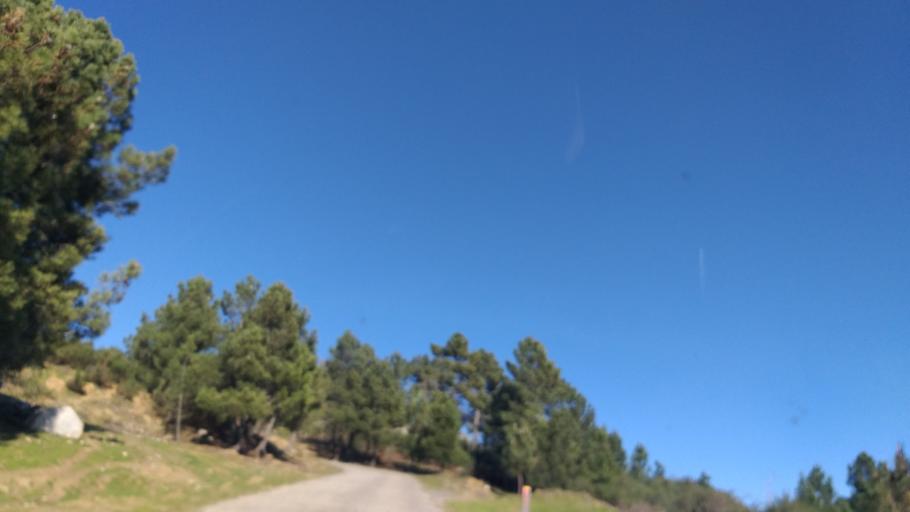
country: PT
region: Guarda
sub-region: Celorico da Beira
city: Celorico da Beira
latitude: 40.5225
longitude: -7.3925
